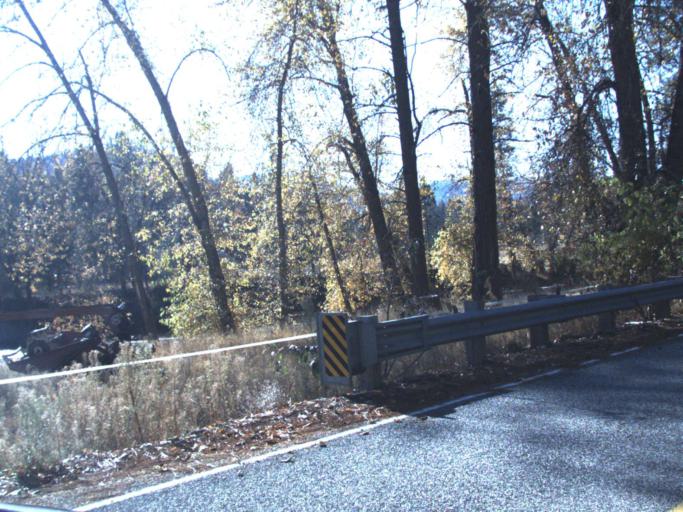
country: CA
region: British Columbia
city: Grand Forks
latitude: 48.9808
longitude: -118.5233
